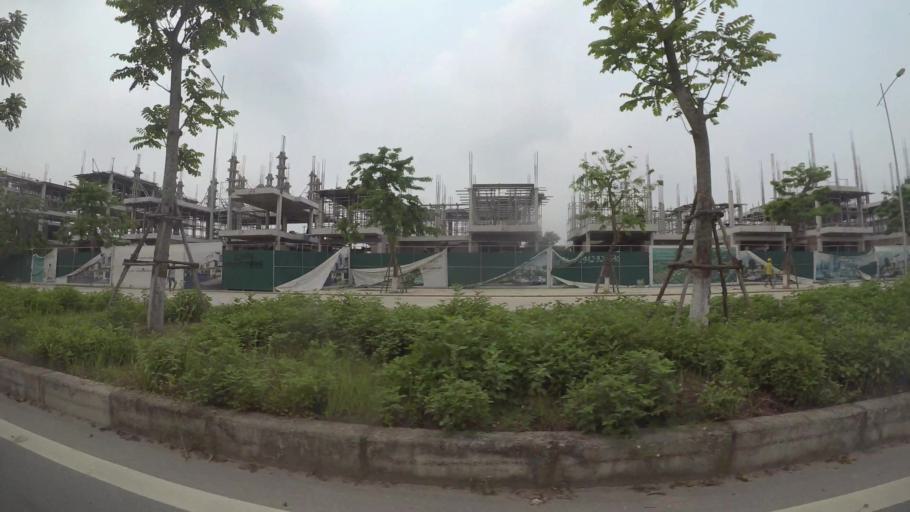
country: VN
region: Ha Noi
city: Ha Dong
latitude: 20.9858
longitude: 105.7541
